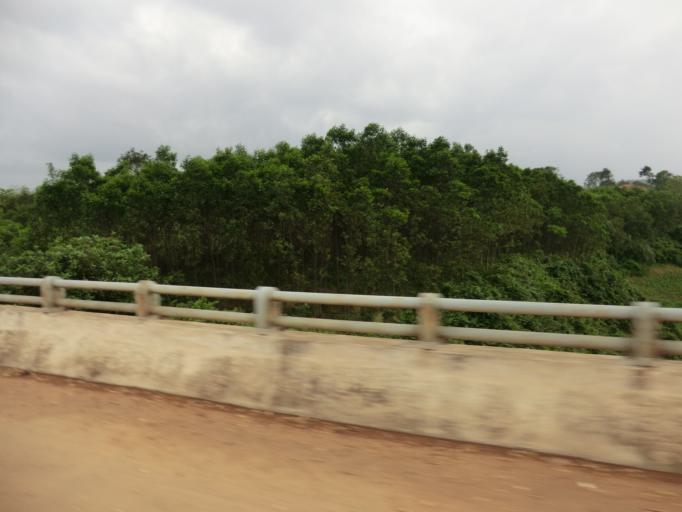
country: VN
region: Quang Tri
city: Ho Xa
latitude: 16.9767
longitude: 106.9354
